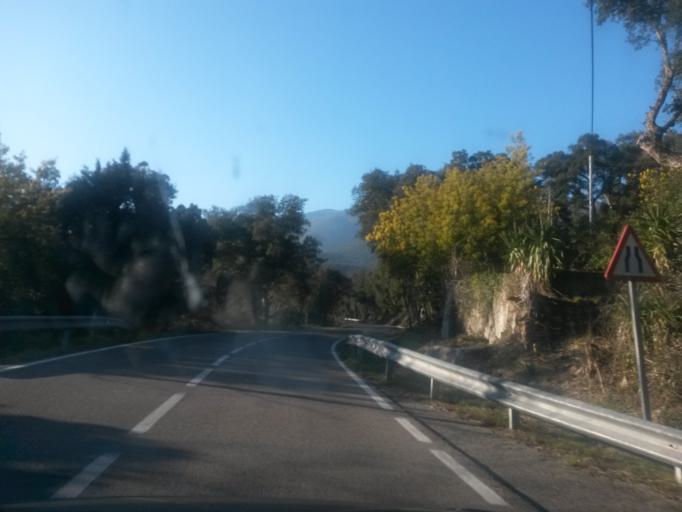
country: ES
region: Catalonia
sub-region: Provincia de Girona
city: Macanet de Cabrenys
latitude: 42.3862
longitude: 2.7854
